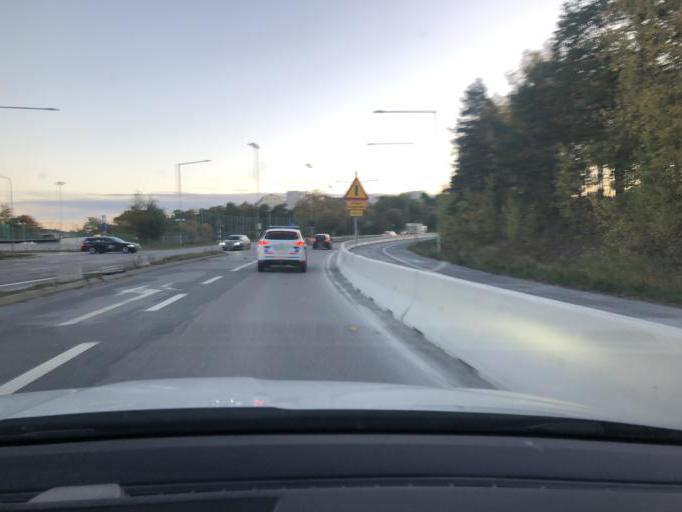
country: SE
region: Stockholm
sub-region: Huddinge Kommun
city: Segeltorp
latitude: 59.2805
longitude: 17.9125
